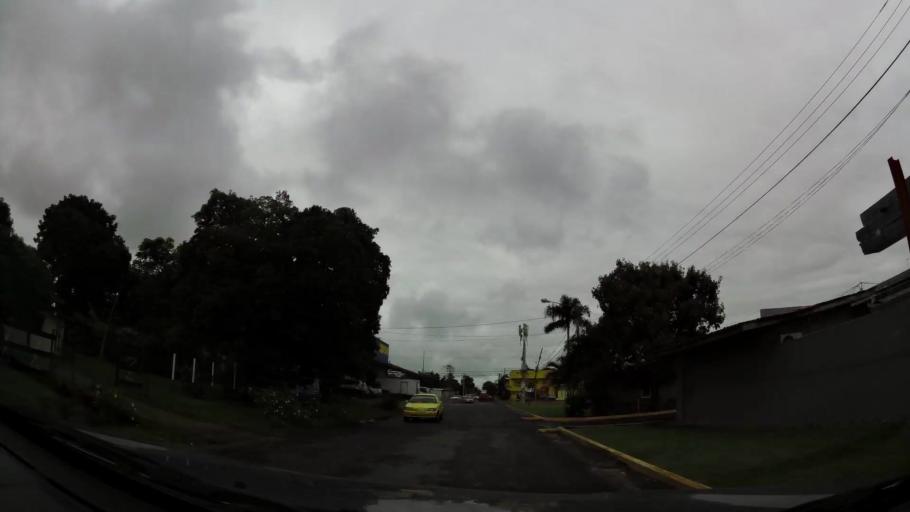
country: PA
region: Chiriqui
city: David
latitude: 8.4347
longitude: -82.4410
